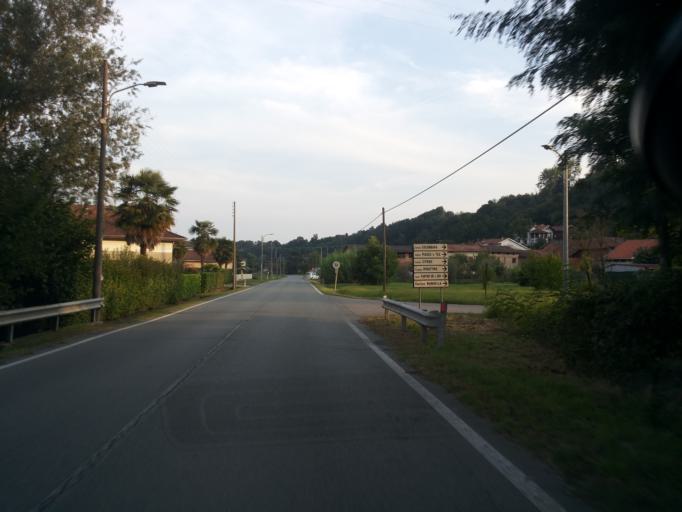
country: IT
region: Piedmont
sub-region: Provincia di Biella
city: Mottalciata
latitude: 45.5203
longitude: 8.1992
